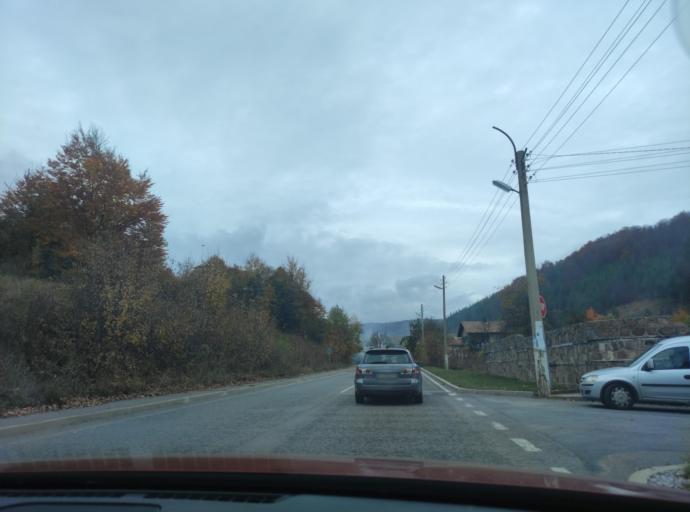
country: BG
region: Sofiya
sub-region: Obshtina Godech
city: Godech
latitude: 43.0848
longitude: 23.1027
